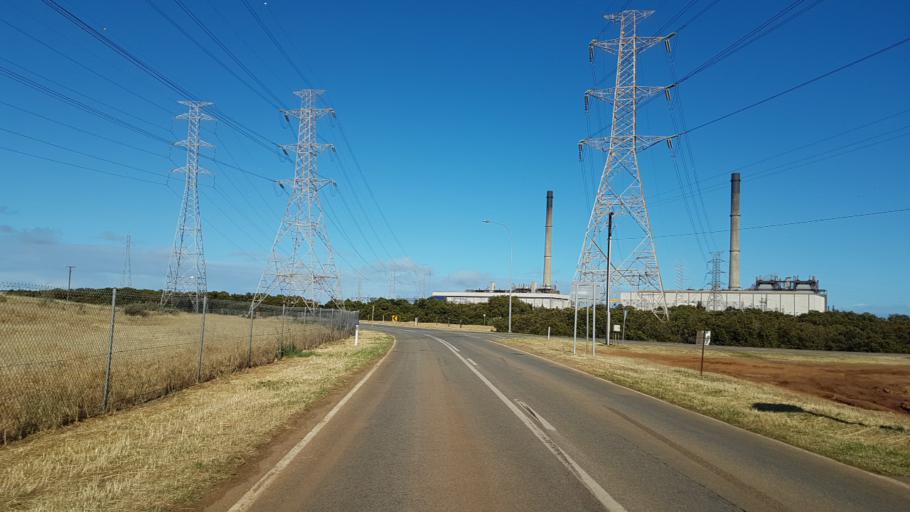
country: AU
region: South Australia
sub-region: Port Adelaide Enfield
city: Birkenhead
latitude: -34.8077
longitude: 138.5304
